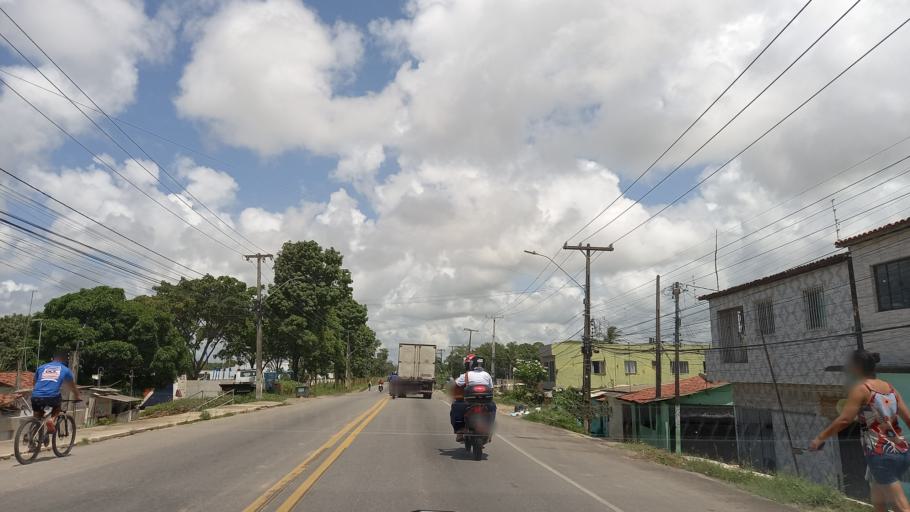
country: BR
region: Pernambuco
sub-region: Jaboatao Dos Guararapes
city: Jaboatao
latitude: -8.2261
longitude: -34.9686
